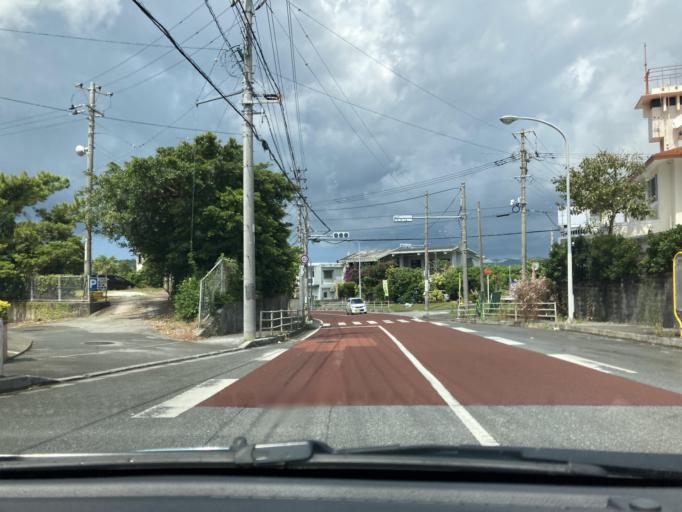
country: JP
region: Okinawa
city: Tomigusuku
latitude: 26.1802
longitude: 127.7427
